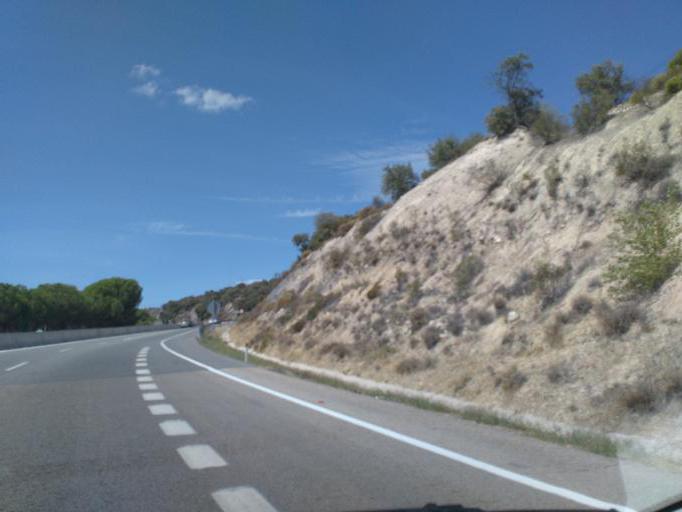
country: ES
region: Madrid
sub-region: Provincia de Madrid
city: Torrelodones
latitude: 40.5302
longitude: -3.9445
